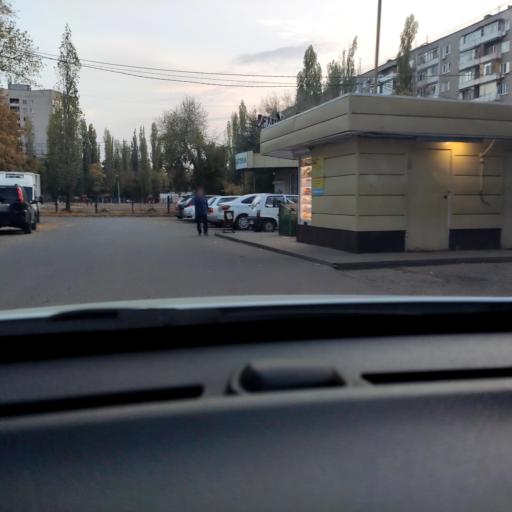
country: RU
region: Voronezj
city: Voronezh
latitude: 51.6710
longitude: 39.2485
